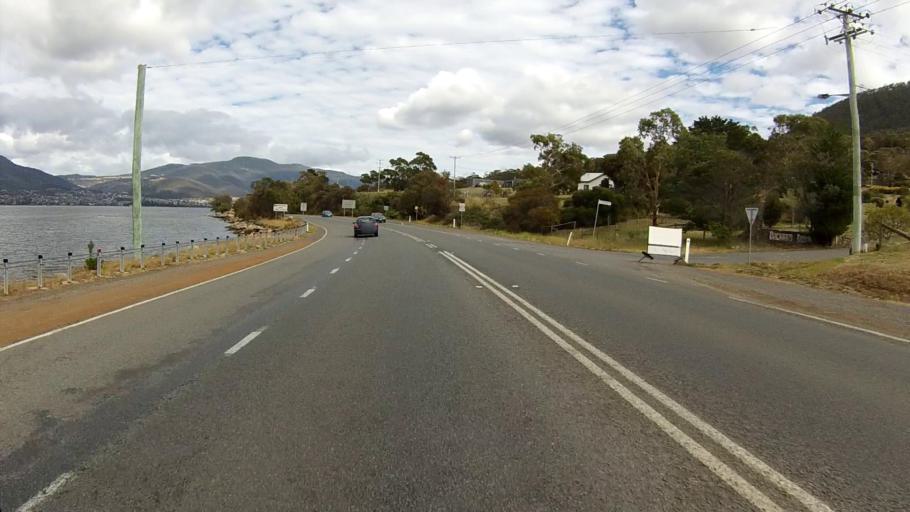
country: AU
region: Tasmania
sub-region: Glenorchy
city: Goodwood
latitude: -42.8122
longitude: 147.3080
